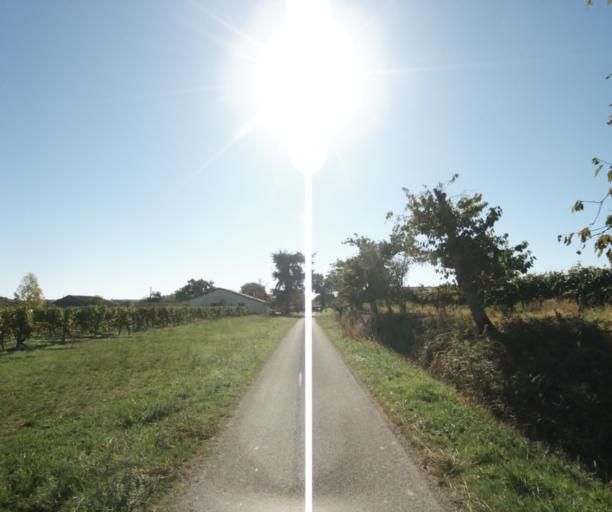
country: FR
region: Midi-Pyrenees
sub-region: Departement du Gers
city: Eauze
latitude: 43.8154
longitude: 0.1413
